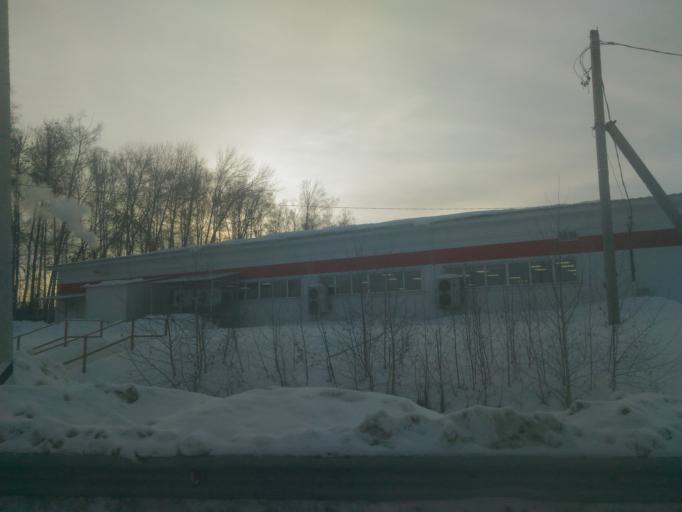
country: RU
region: Ulyanovsk
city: Isheyevka
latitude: 54.4279
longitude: 48.2755
